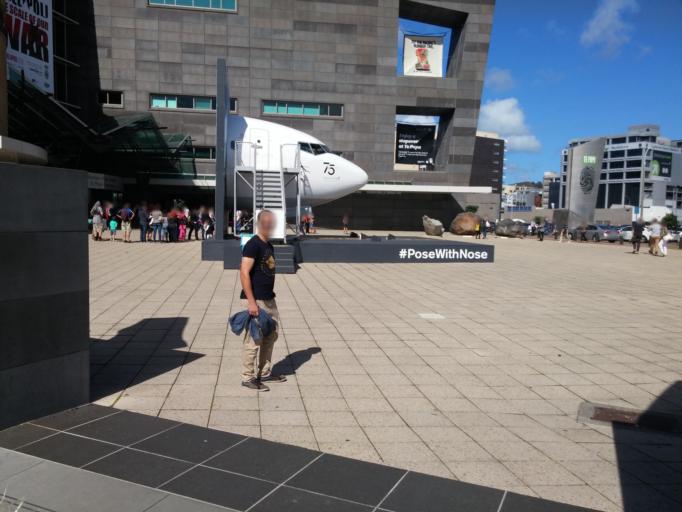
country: NZ
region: Wellington
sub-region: Wellington City
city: Wellington
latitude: -41.2902
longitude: 174.7809
